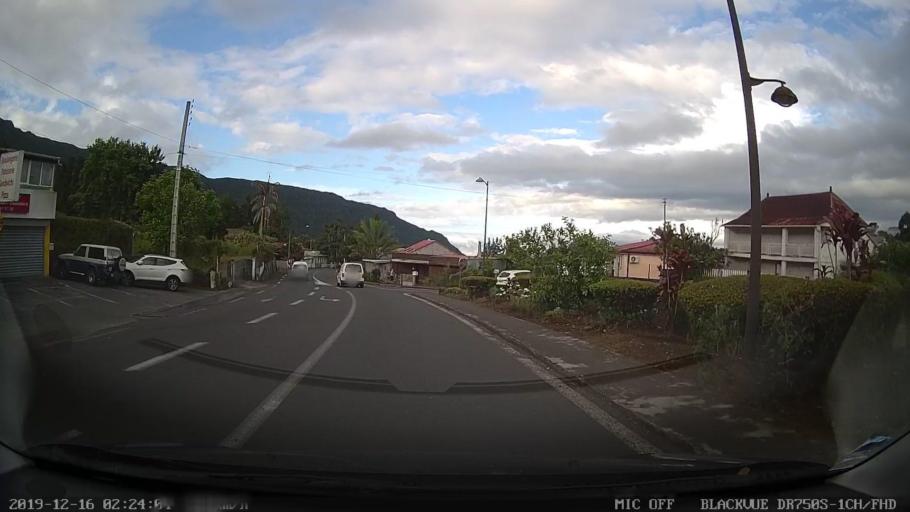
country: RE
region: Reunion
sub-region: Reunion
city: Saint-Benoit
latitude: -21.1399
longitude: 55.6228
